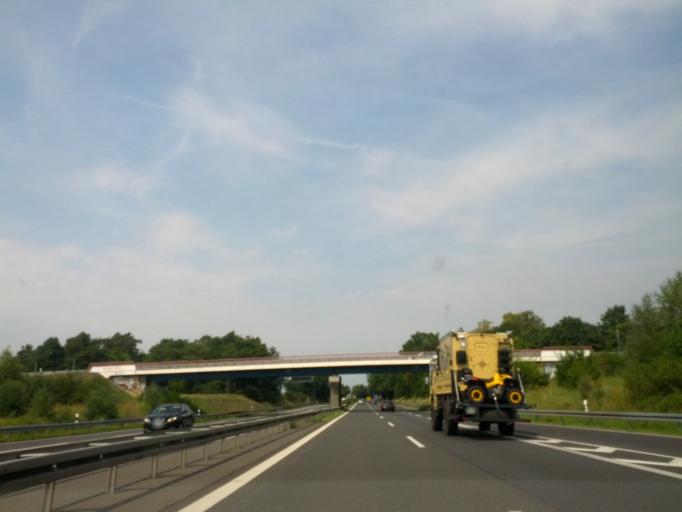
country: DE
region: Brandenburg
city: Werder
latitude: 52.4339
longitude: 12.9302
